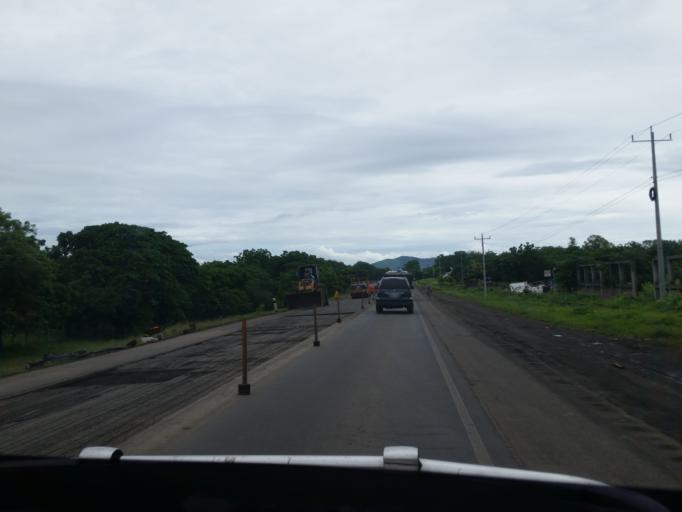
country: NI
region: Managua
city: Tipitapa
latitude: 12.2823
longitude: -86.0629
